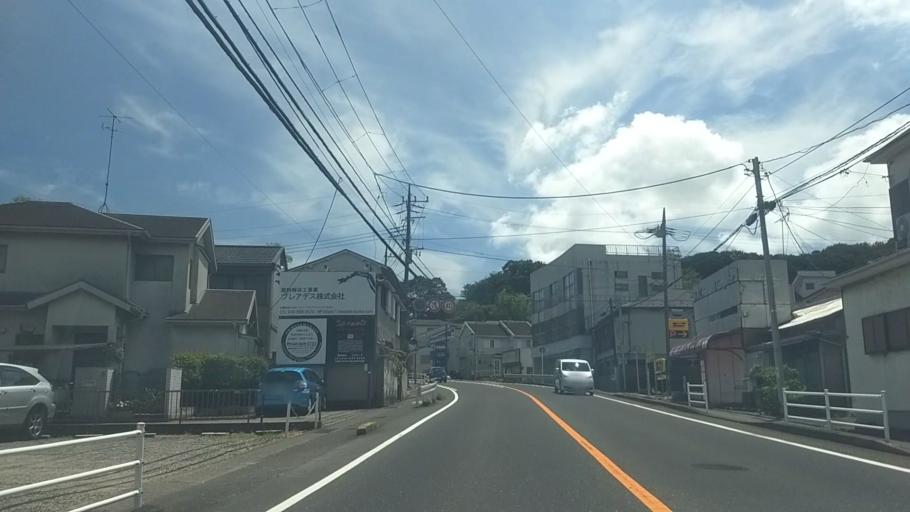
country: JP
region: Kanagawa
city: Yokosuka
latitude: 35.2542
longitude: 139.6654
